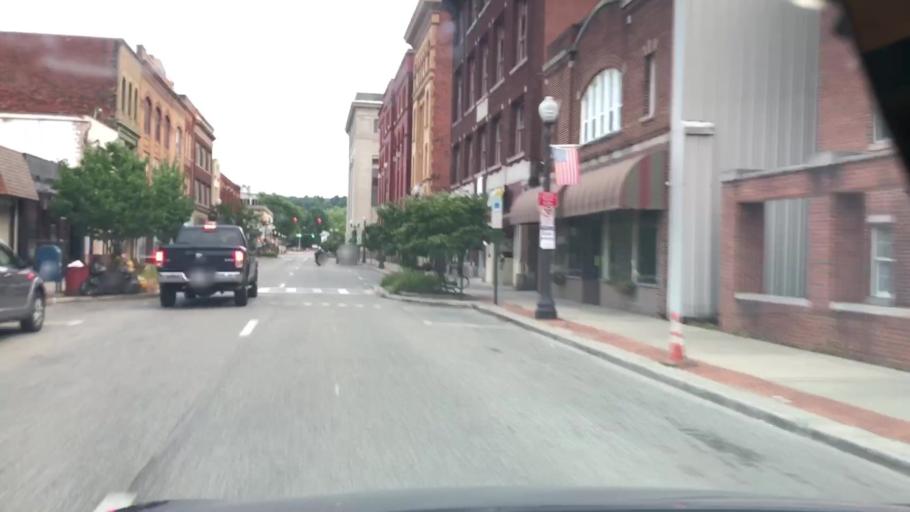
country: US
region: Pennsylvania
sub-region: Venango County
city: Oil City
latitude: 41.4352
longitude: -79.7088
